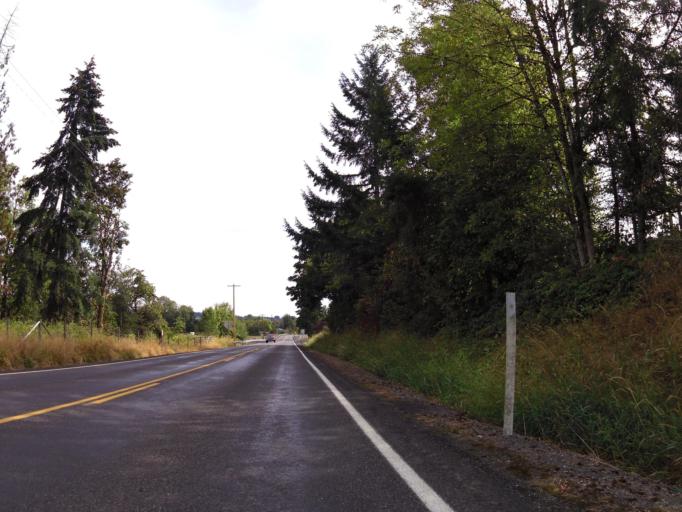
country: US
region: Washington
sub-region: Lewis County
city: Chehalis
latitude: 46.6413
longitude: -122.9772
